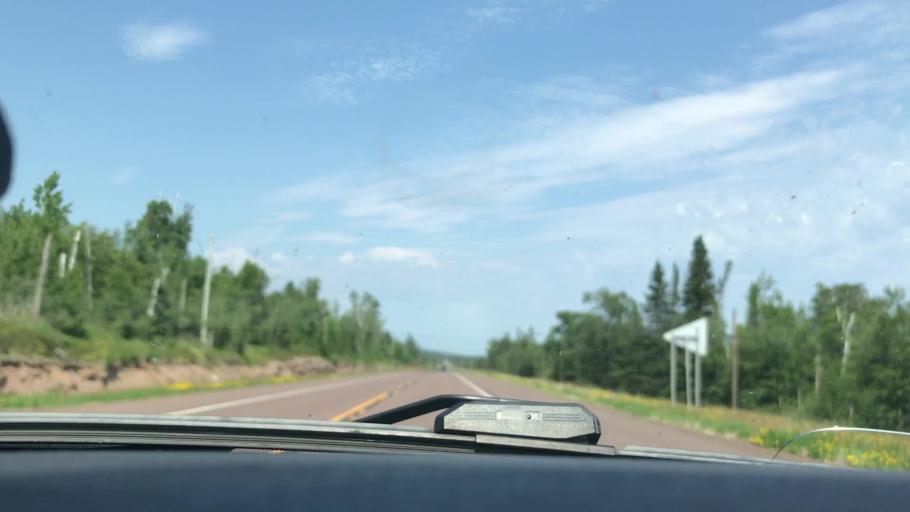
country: US
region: Minnesota
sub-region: Cook County
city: Grand Marais
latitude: 47.6210
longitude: -90.7479
